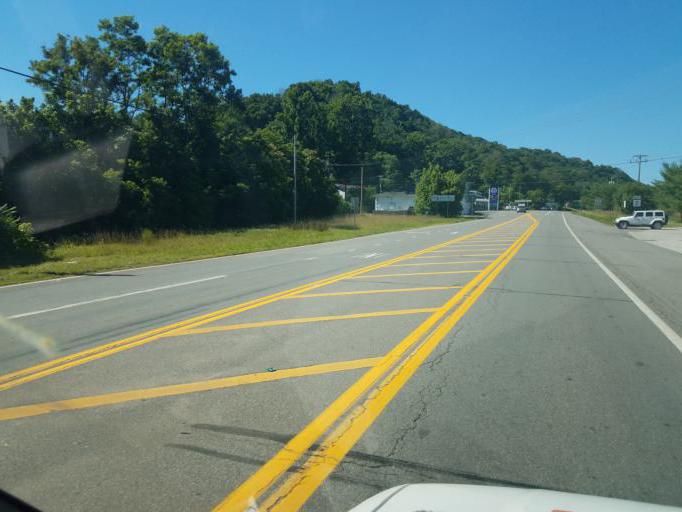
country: US
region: West Virginia
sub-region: Cabell County
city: Lesage
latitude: 38.4610
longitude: -82.3028
